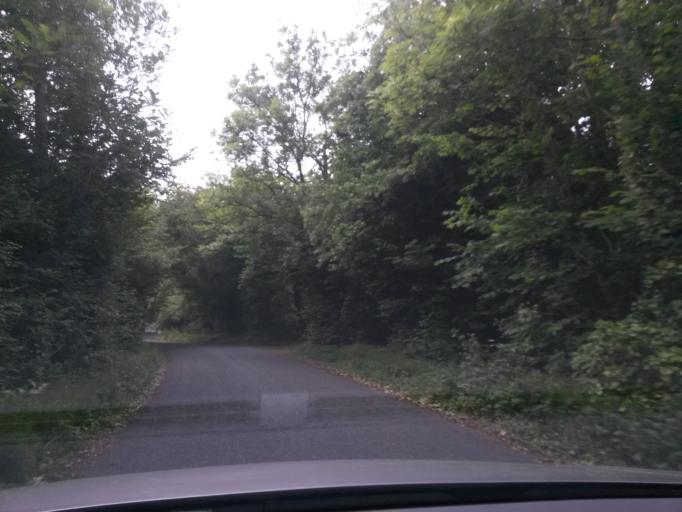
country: IE
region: Connaught
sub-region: Sligo
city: Sligo
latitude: 54.2424
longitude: -8.4439
